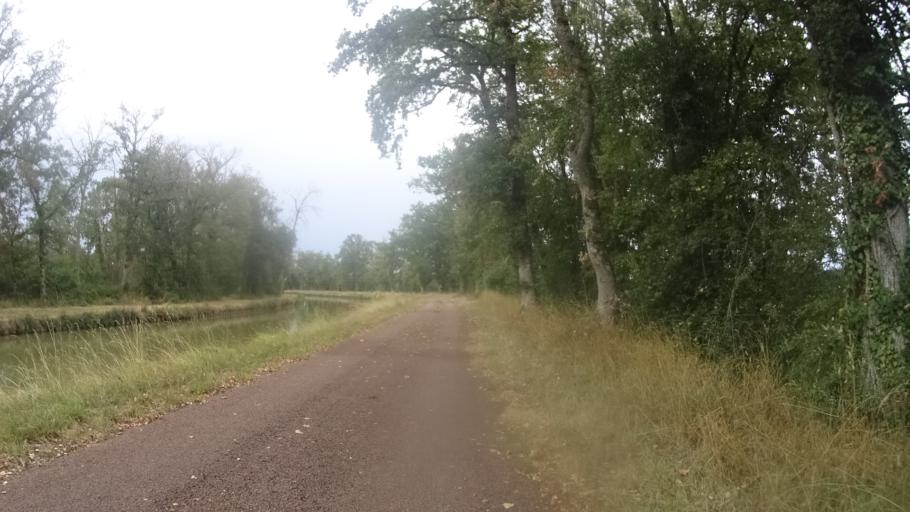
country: FR
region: Bourgogne
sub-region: Departement de la Nievre
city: Imphy
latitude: 46.9058
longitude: 3.2486
